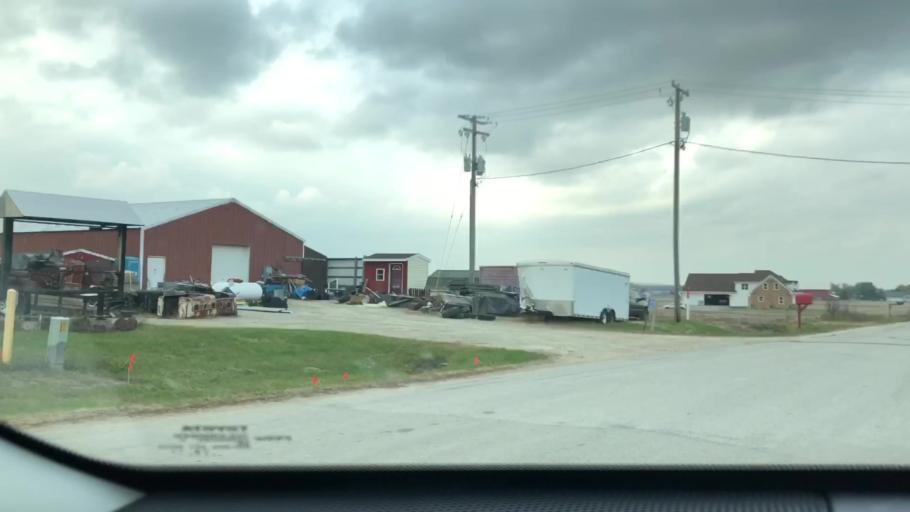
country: US
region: Wisconsin
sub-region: Outagamie County
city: Seymour
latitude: 44.5006
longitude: -88.3106
